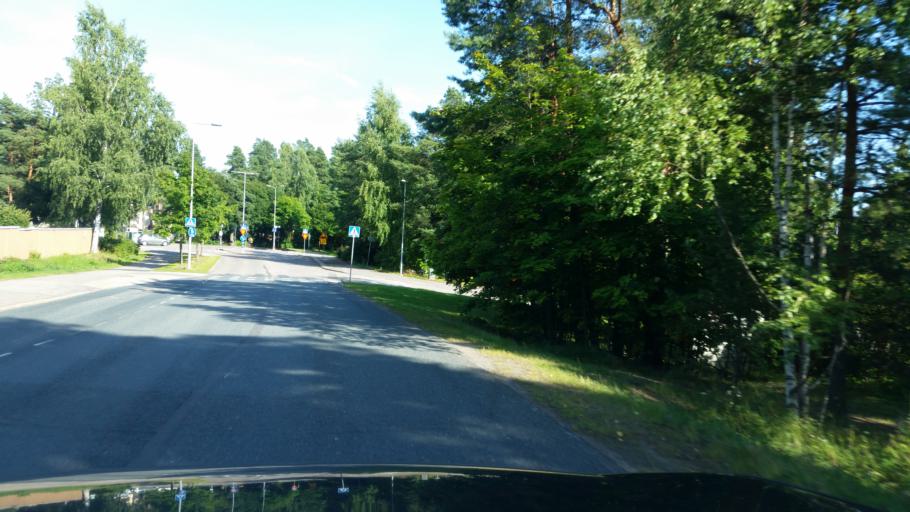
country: FI
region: Uusimaa
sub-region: Helsinki
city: Vantaa
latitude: 60.3153
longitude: 25.0118
